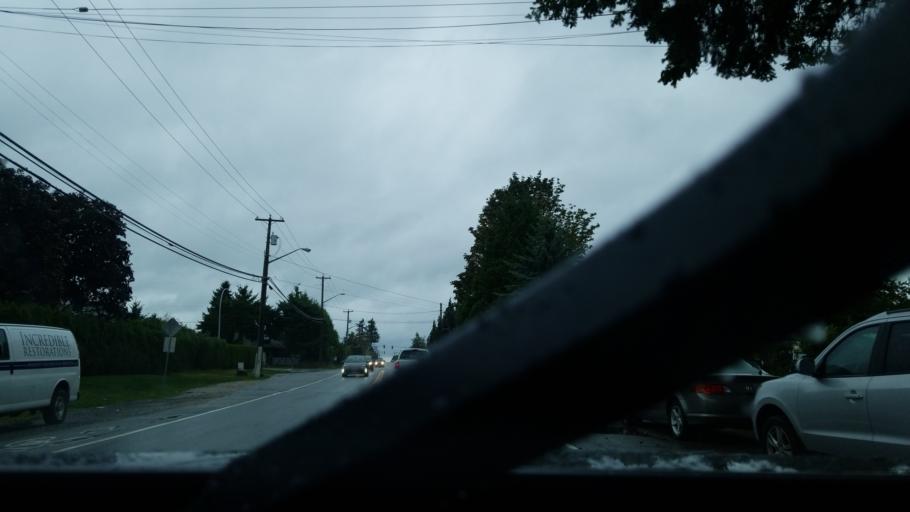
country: CA
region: British Columbia
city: Langley
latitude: 49.1191
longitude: -122.6951
